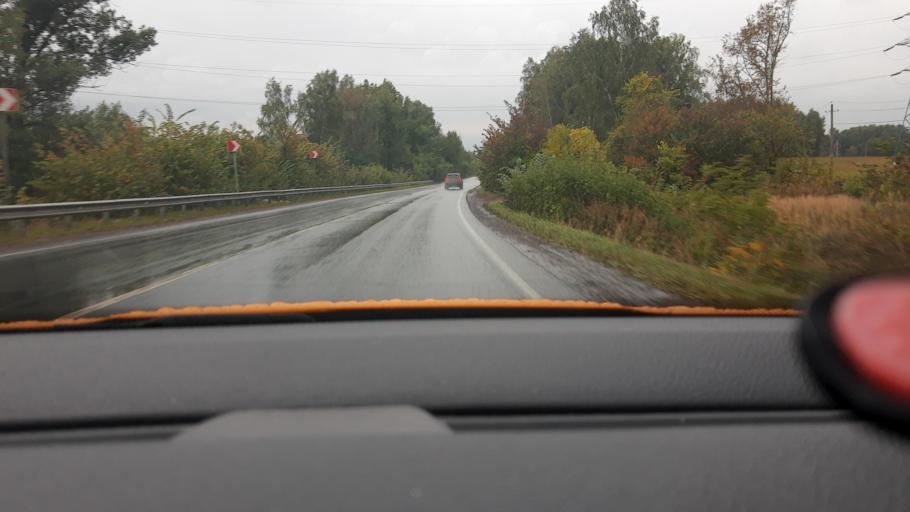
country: RU
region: Moskovskaya
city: Obukhovo
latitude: 55.8066
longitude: 38.2513
